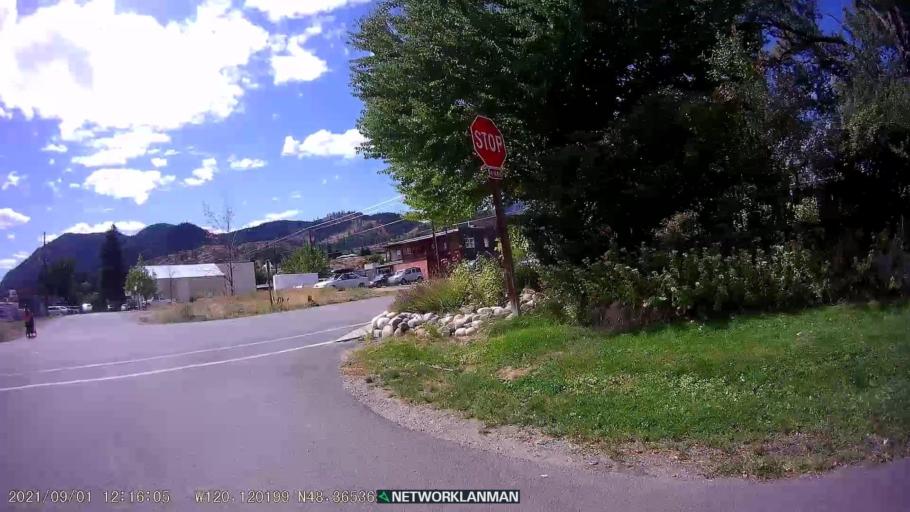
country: US
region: Washington
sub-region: Okanogan County
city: Brewster
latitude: 48.3652
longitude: -120.1203
